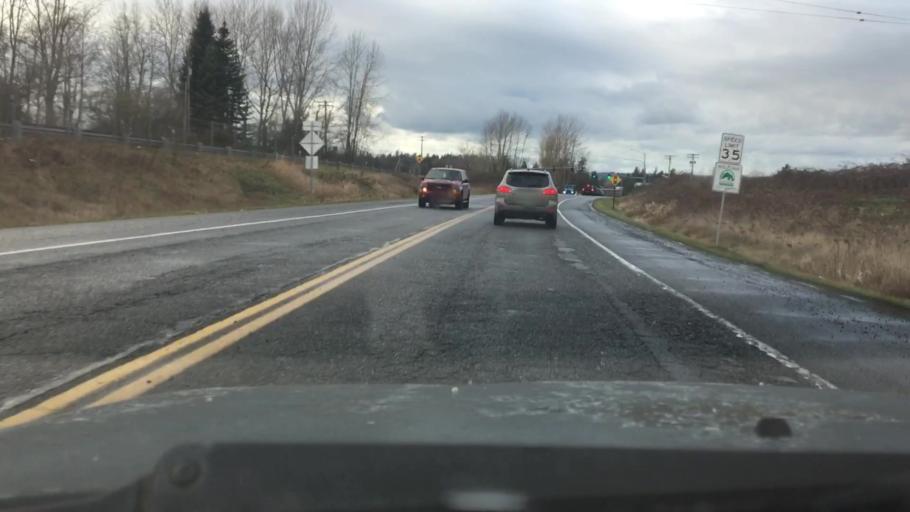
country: US
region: Washington
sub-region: Whatcom County
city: Marietta-Alderwood
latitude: 48.8171
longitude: -122.5517
